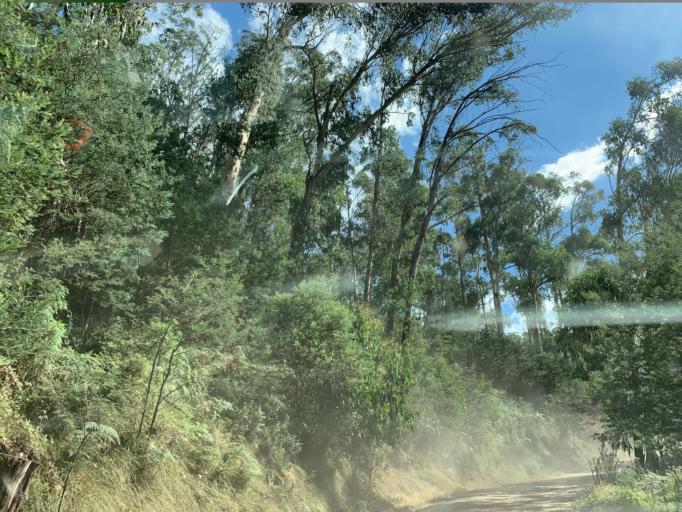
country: AU
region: Victoria
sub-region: Mansfield
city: Mansfield
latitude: -37.0994
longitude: 146.5133
